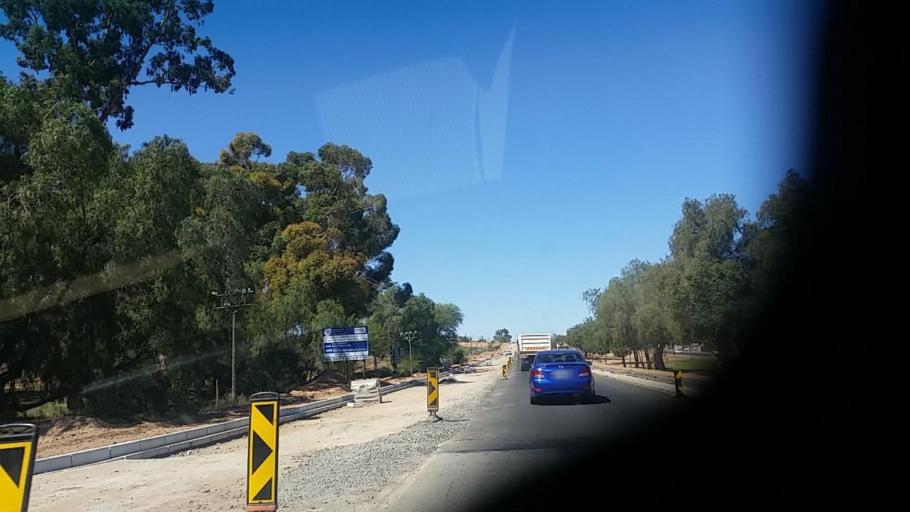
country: ZA
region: Western Cape
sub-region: Eden District Municipality
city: Oudtshoorn
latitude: -33.5942
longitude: 22.2228
